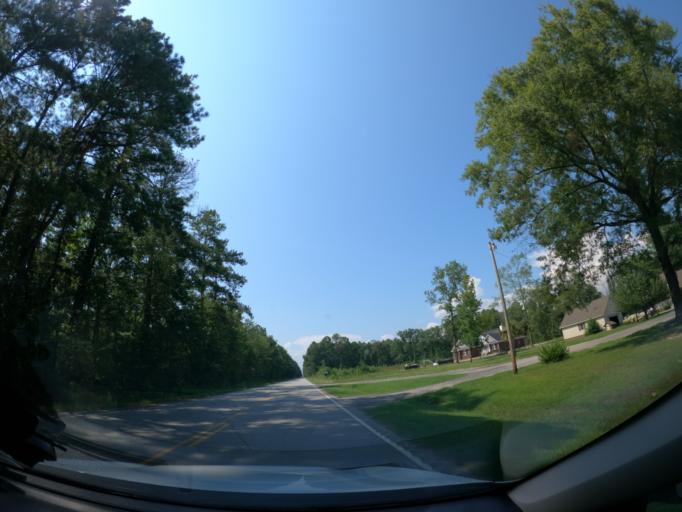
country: US
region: South Carolina
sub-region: Richland County
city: Hopkins
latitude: 33.8687
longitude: -80.8920
